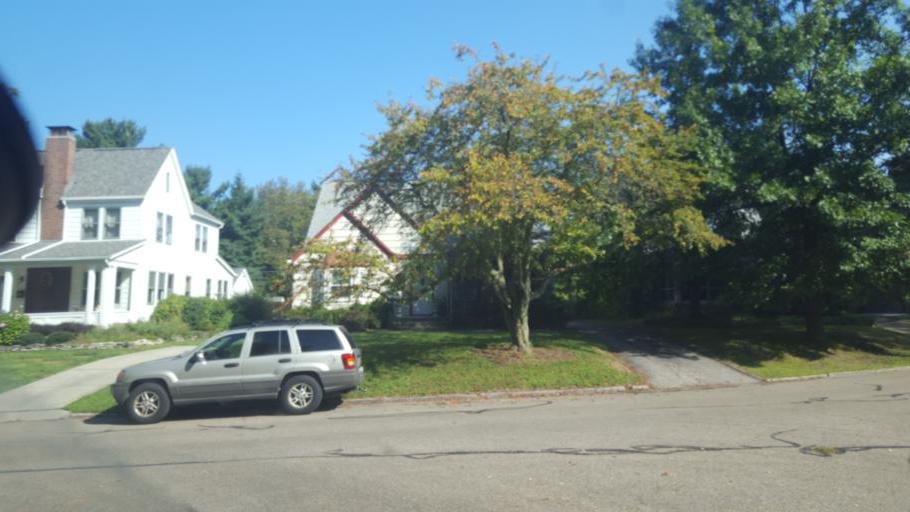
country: US
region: Ohio
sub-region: Franklin County
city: Grandview Heights
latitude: 40.0299
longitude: -83.0050
